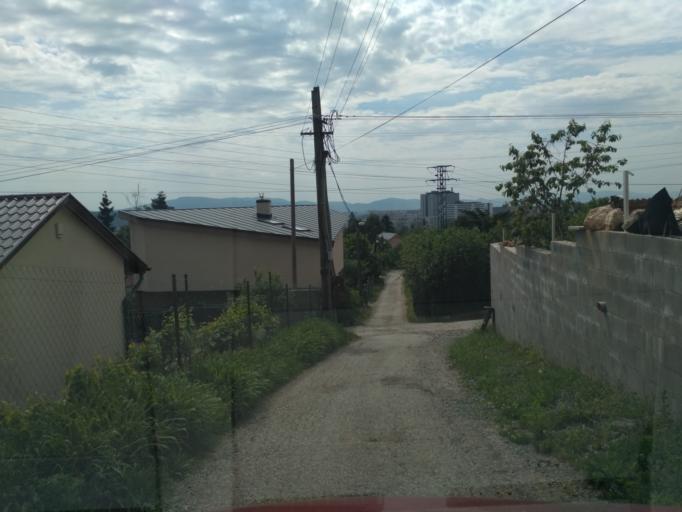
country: SK
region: Kosicky
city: Kosice
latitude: 48.7341
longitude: 21.2310
